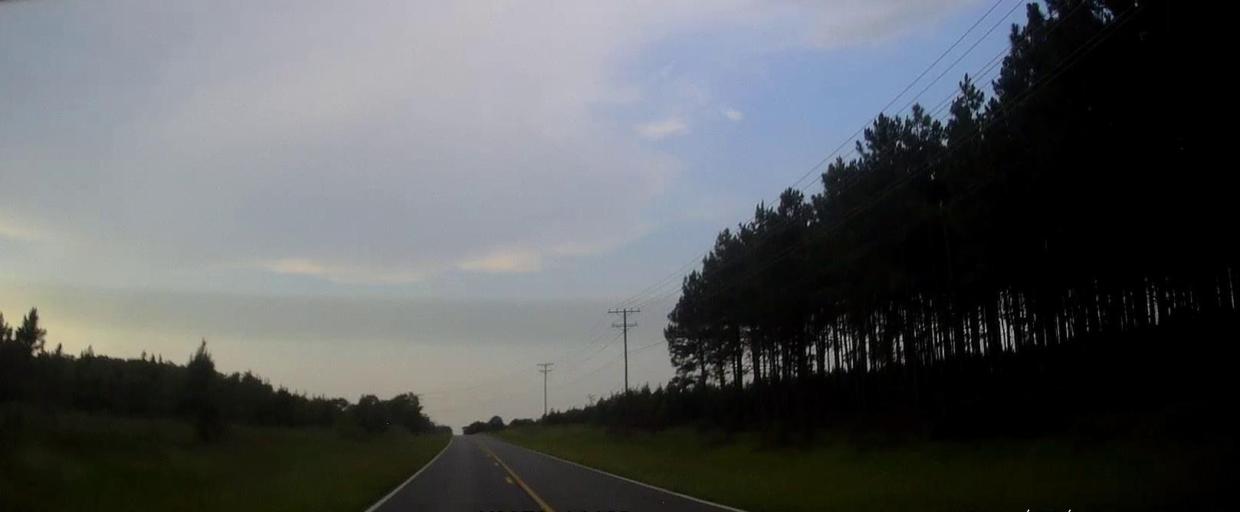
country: US
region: Georgia
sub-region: Laurens County
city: East Dublin
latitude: 32.5449
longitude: -82.8367
